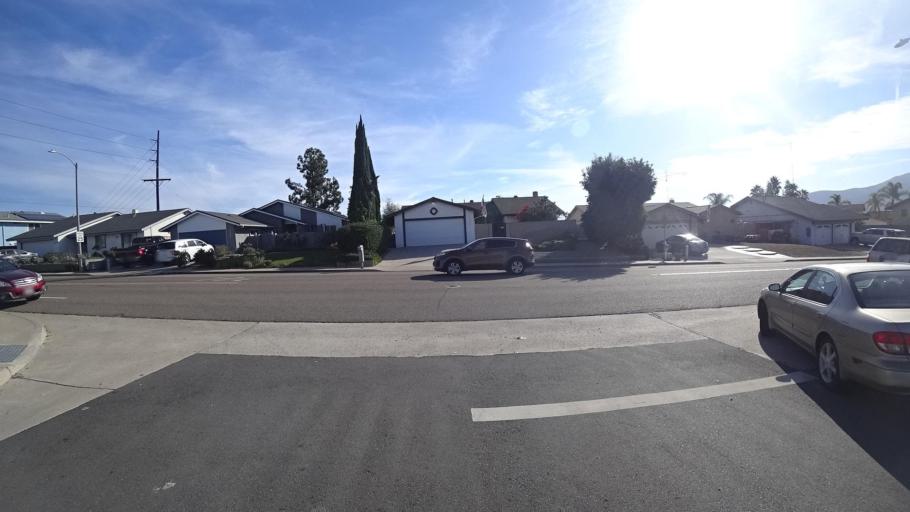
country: US
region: California
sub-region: San Diego County
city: Casa de Oro-Mount Helix
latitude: 32.7399
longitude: -116.9611
